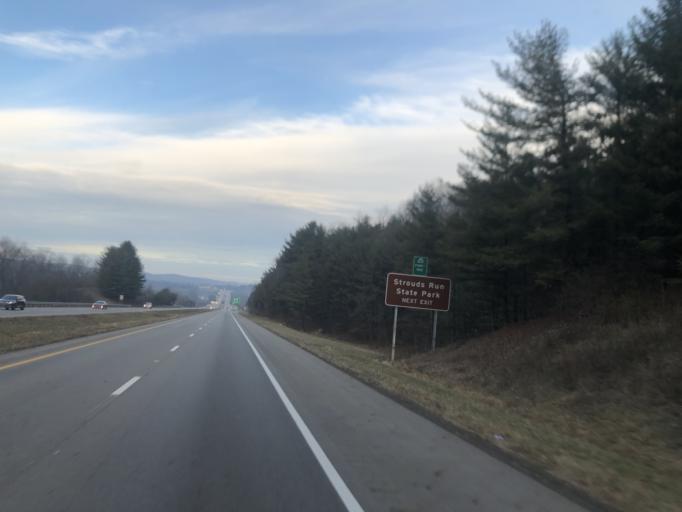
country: US
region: Ohio
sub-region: Athens County
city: Athens
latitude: 39.3571
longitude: -82.0987
